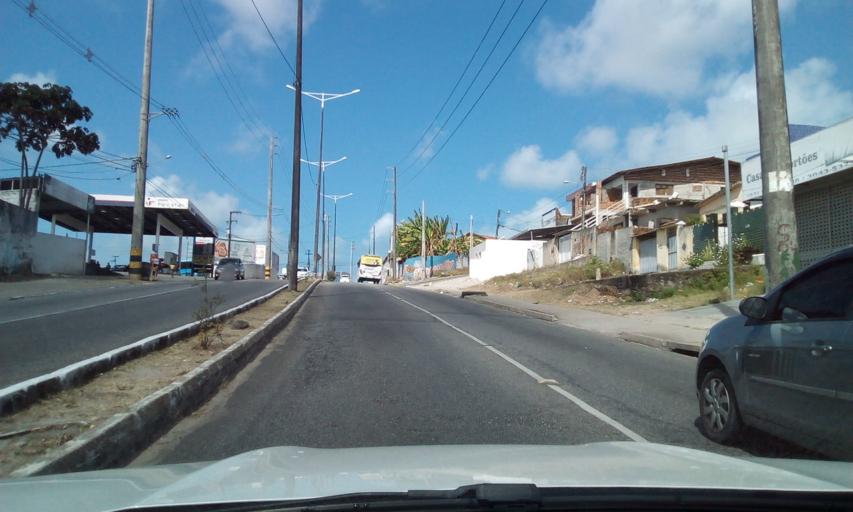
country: BR
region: Paraiba
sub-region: Joao Pessoa
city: Joao Pessoa
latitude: -7.1046
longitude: -34.8649
